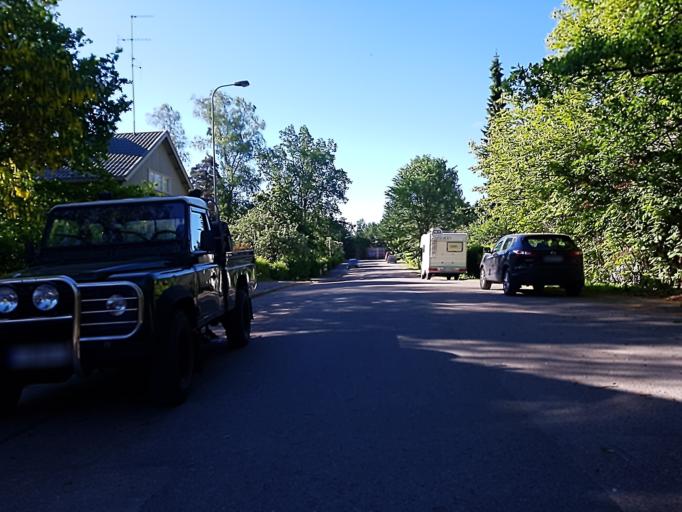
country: FI
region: Uusimaa
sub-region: Helsinki
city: Helsinki
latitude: 60.2408
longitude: 24.9151
